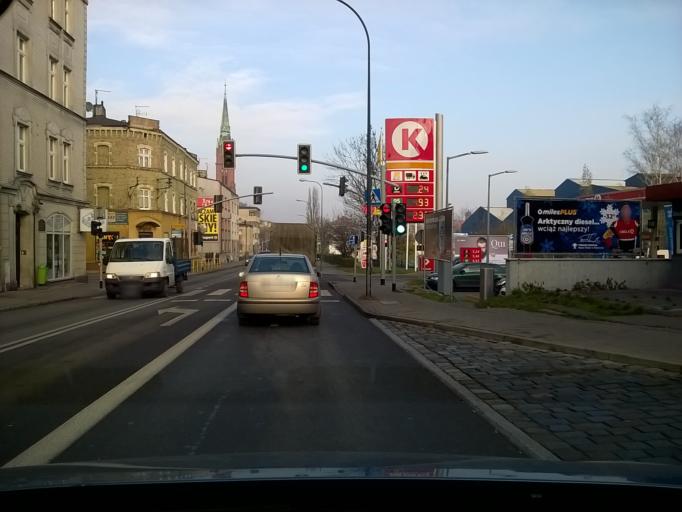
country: PL
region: Silesian Voivodeship
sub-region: Swietochlowice
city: Swietochlowice
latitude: 50.2715
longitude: 18.9384
